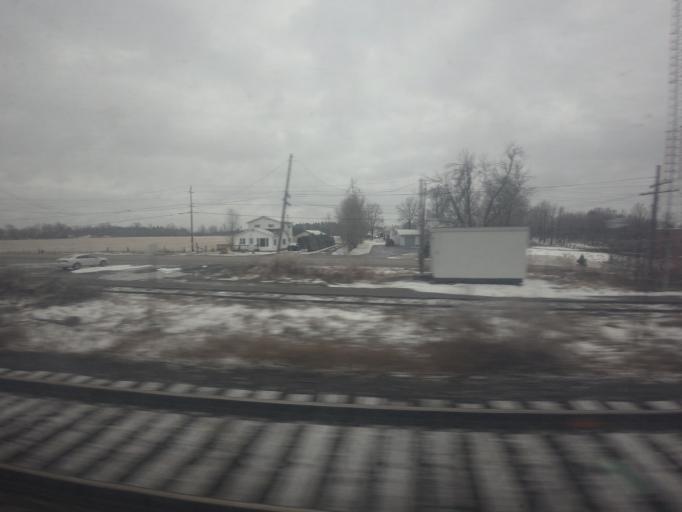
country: CA
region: Ontario
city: Gananoque
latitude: 44.3687
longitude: -76.1548
